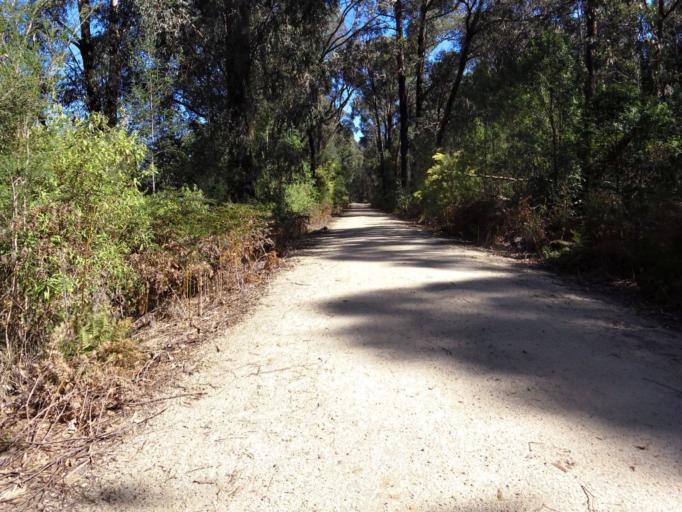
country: AU
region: Victoria
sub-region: Latrobe
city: Moe
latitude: -38.3814
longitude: 146.1927
